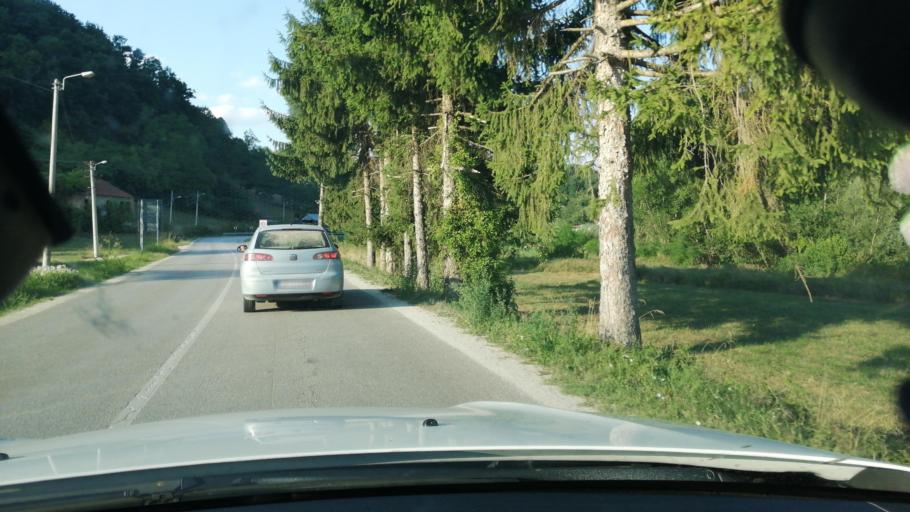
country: RS
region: Central Serbia
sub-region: Moravicki Okrug
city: Lucani
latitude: 43.7898
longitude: 20.2342
